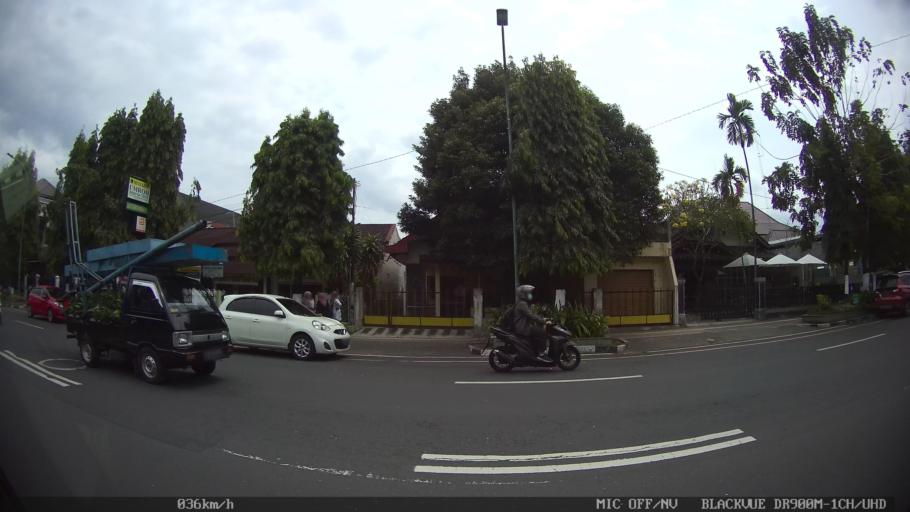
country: ID
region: Daerah Istimewa Yogyakarta
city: Yogyakarta
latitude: -7.8013
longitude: 110.3920
